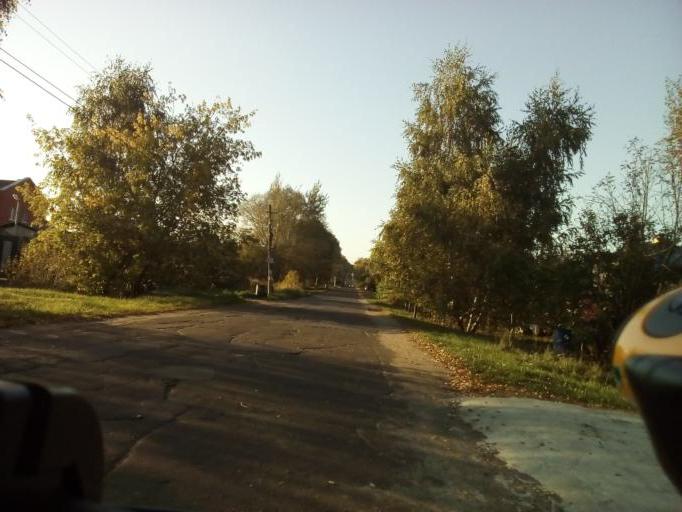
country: RU
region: Moskovskaya
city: Ramenskoye
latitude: 55.6076
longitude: 38.3025
